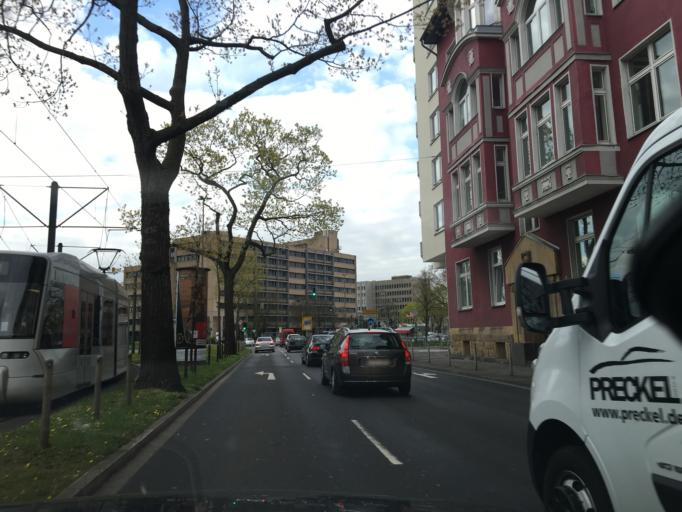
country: DE
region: North Rhine-Westphalia
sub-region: Regierungsbezirk Dusseldorf
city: Dusseldorf
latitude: 51.2493
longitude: 6.8022
